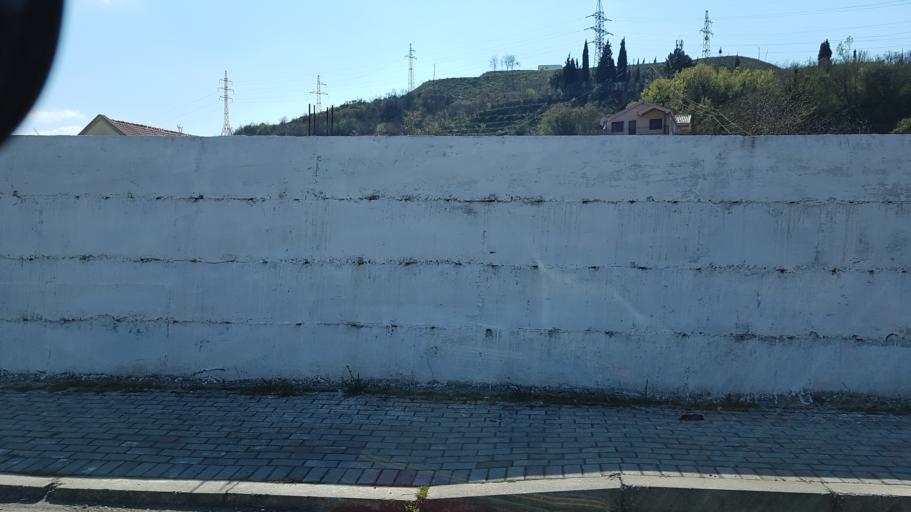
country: AL
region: Shkoder
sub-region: Rrethi i Shkodres
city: Shkoder
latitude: 42.0561
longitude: 19.5098
